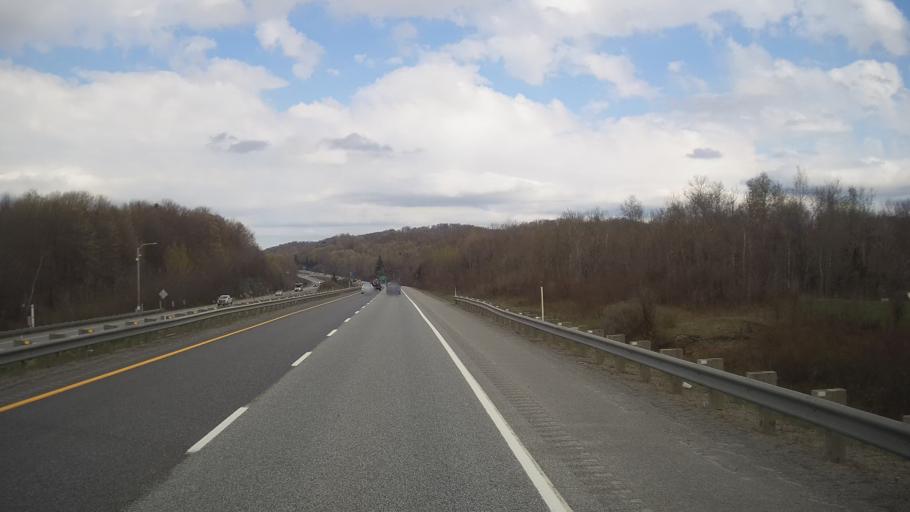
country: CA
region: Quebec
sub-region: Estrie
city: Magog
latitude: 45.2896
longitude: -72.2619
